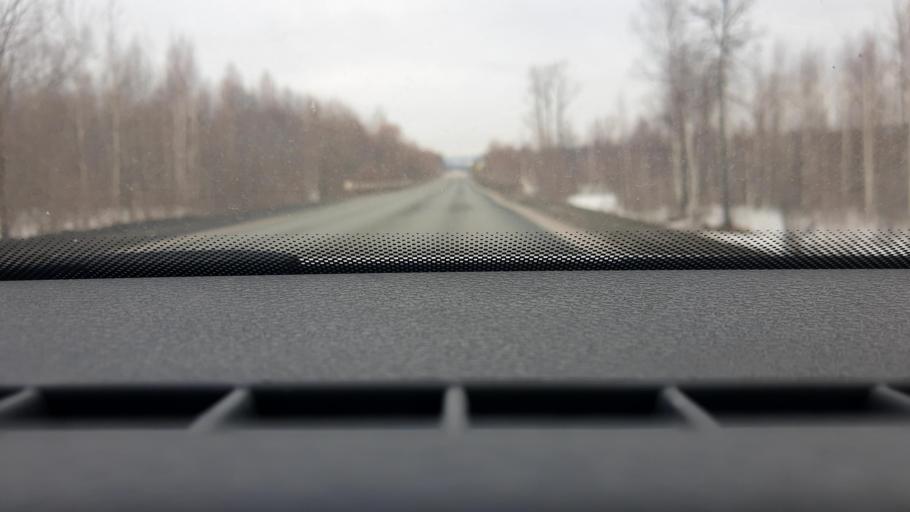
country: RU
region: Chelyabinsk
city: Asha
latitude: 54.9256
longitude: 57.2893
